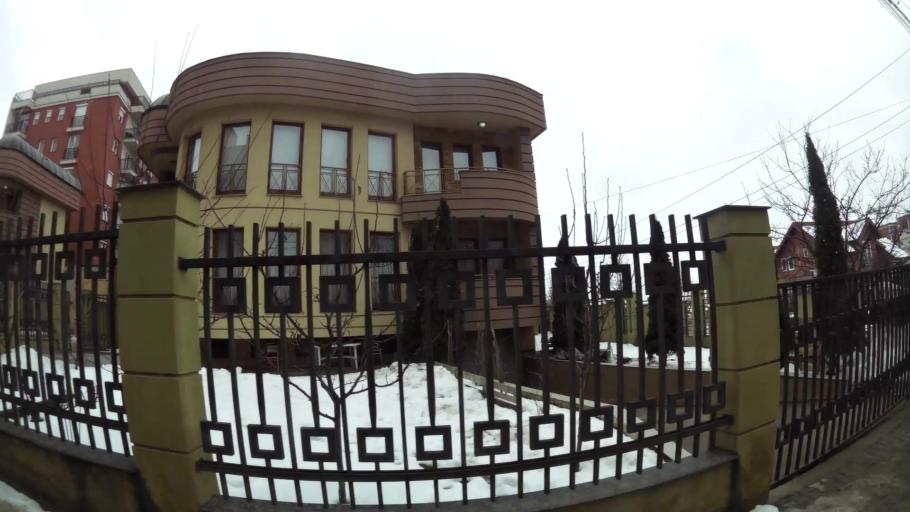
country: XK
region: Pristina
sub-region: Komuna e Prishtines
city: Pristina
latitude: 42.6541
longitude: 21.1839
